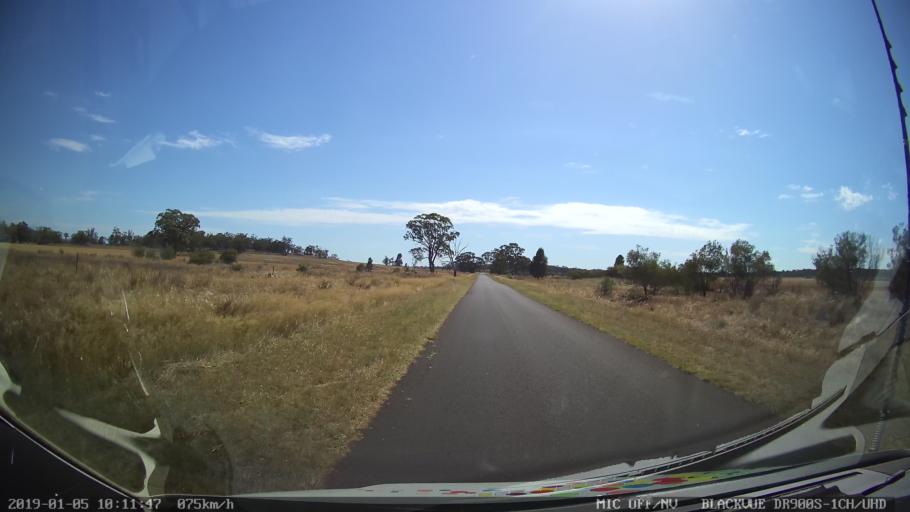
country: AU
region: New South Wales
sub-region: Gilgandra
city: Gilgandra
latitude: -31.6114
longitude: 148.9053
